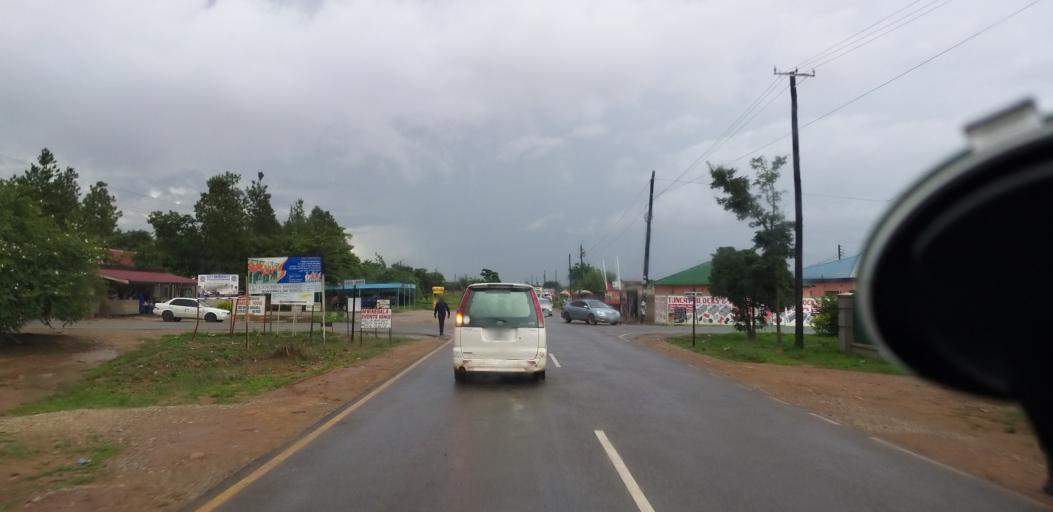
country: ZM
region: Lusaka
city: Lusaka
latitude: -15.4774
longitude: 28.3161
